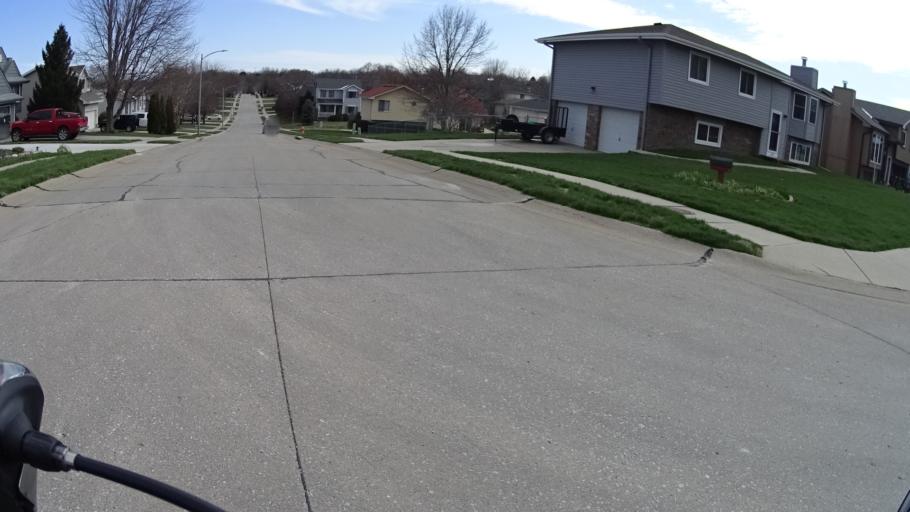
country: US
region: Nebraska
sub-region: Sarpy County
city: Offutt Air Force Base
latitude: 41.1114
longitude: -95.9613
